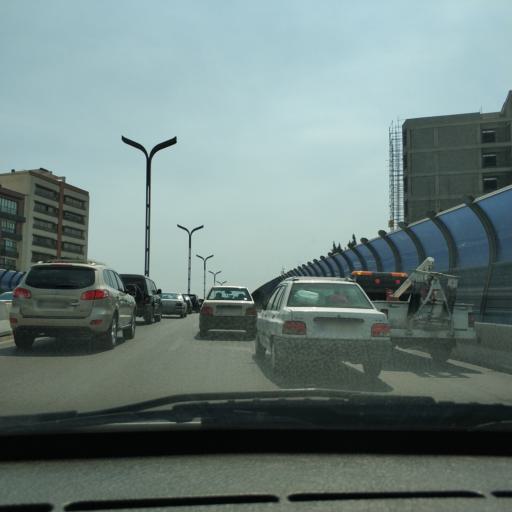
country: IR
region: Tehran
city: Tajrish
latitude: 35.7883
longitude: 51.4508
